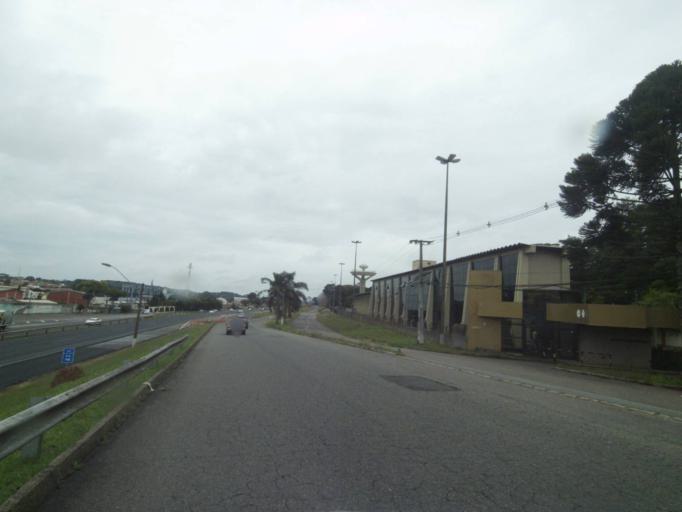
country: BR
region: Parana
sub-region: Curitiba
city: Curitiba
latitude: -25.4306
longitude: -49.3508
